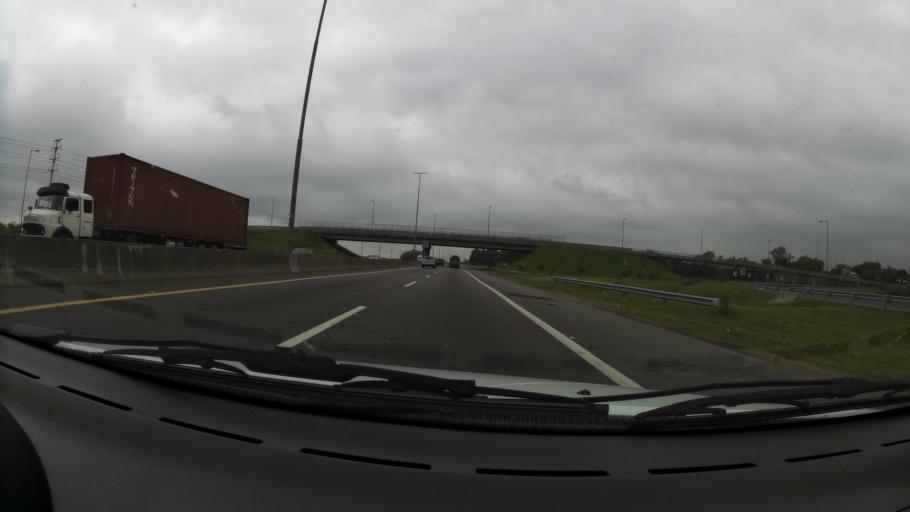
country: AR
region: Buenos Aires
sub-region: Partido de Quilmes
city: Quilmes
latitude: -34.7873
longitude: -58.1453
